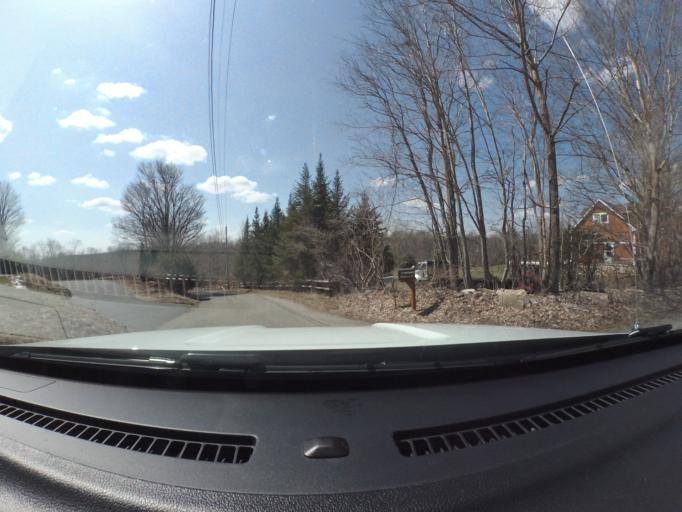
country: US
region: Connecticut
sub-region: Litchfield County
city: Bethlehem Village
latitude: 41.6298
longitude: -73.1617
